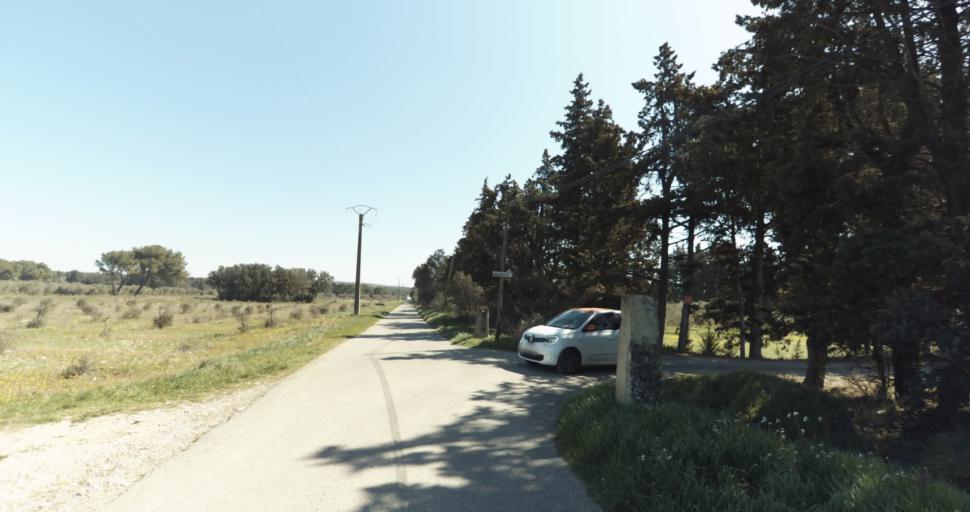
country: FR
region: Provence-Alpes-Cote d'Azur
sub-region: Departement des Bouches-du-Rhone
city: Pelissanne
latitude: 43.6117
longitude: 5.1512
